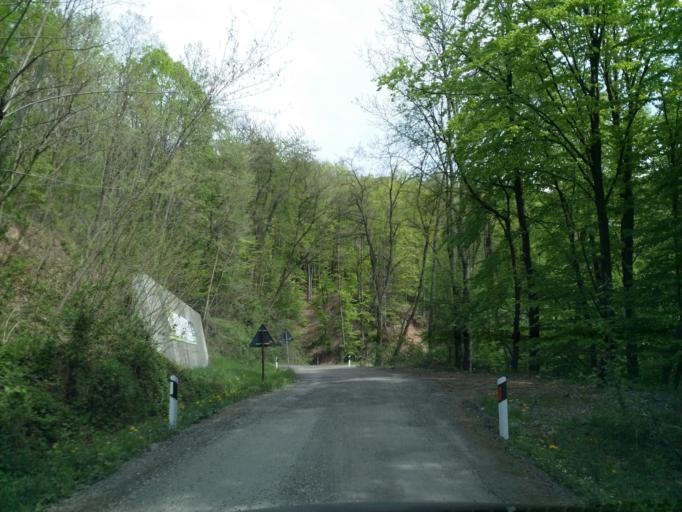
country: RS
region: Central Serbia
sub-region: Pomoravski Okrug
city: Despotovac
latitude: 43.9623
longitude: 21.5621
